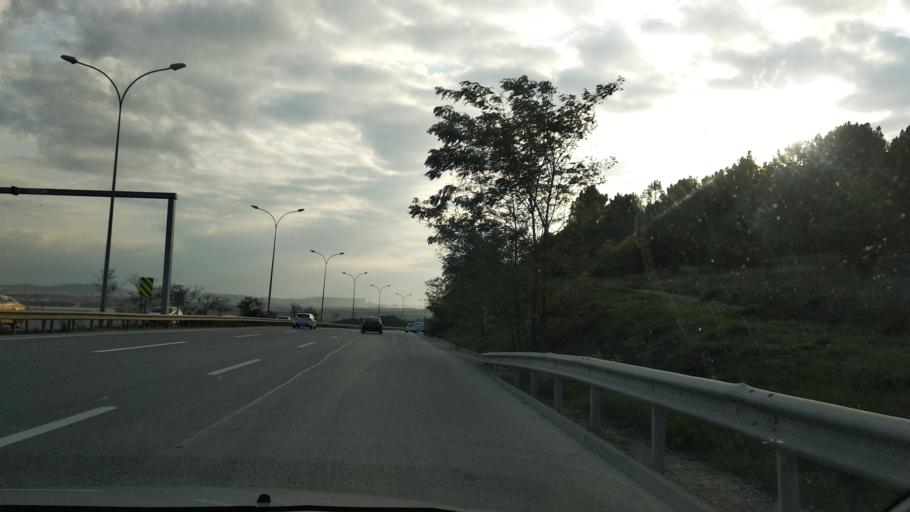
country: TR
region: Istanbul
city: Pendik
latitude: 40.9202
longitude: 29.3391
